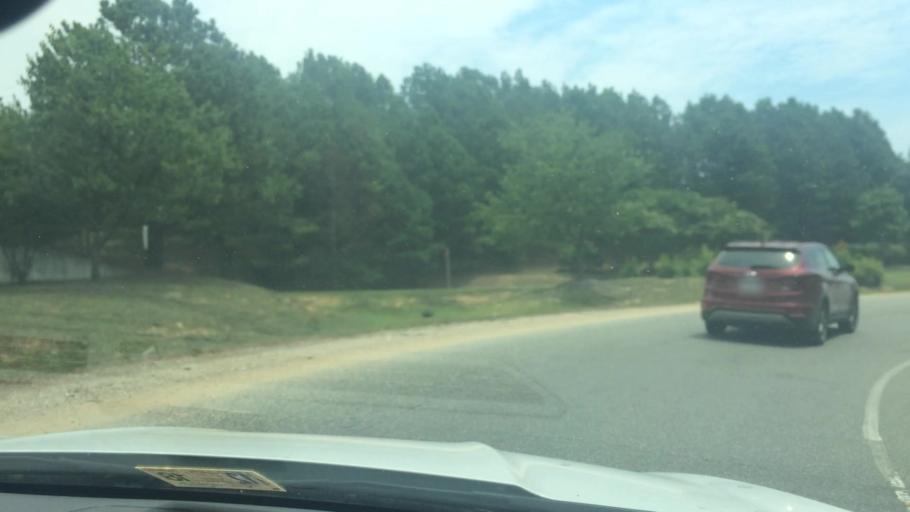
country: US
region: Virginia
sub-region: James City County
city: Williamsburg
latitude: 37.2723
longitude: -76.7529
